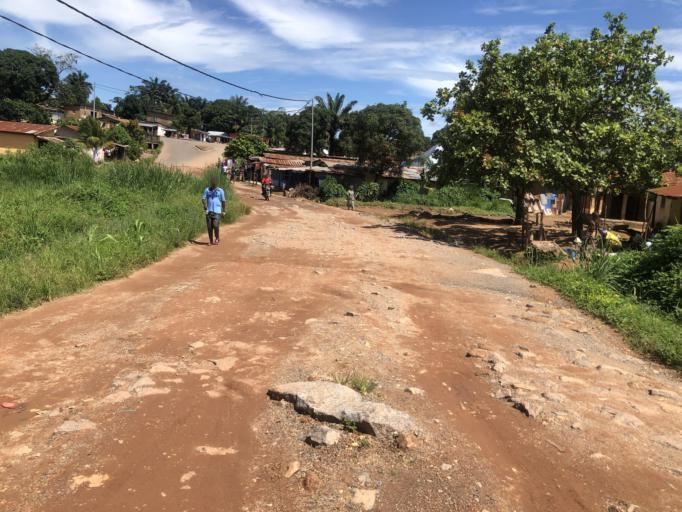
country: SL
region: Eastern Province
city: Koidu
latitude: 8.6455
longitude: -10.9548
